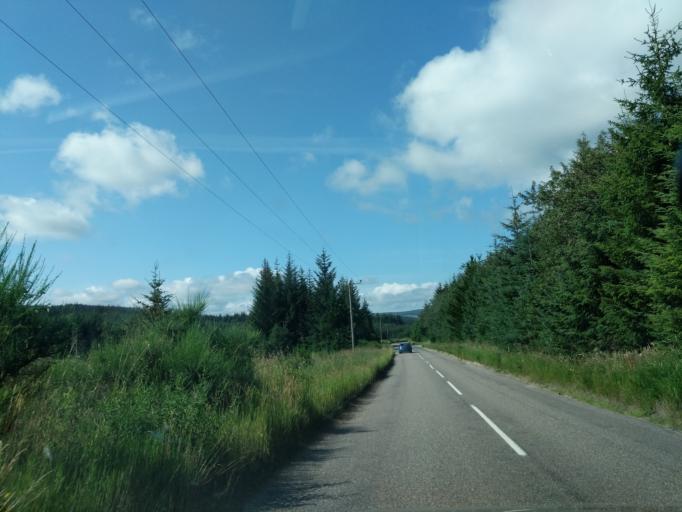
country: GB
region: Scotland
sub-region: Moray
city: Dufftown
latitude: 57.3648
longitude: -3.2658
